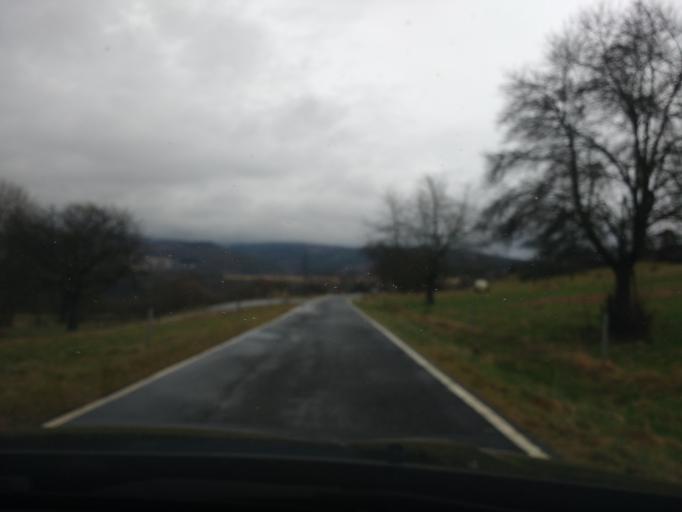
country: DE
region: Rheinland-Pfalz
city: Ollmuth
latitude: 49.6739
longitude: 6.7086
